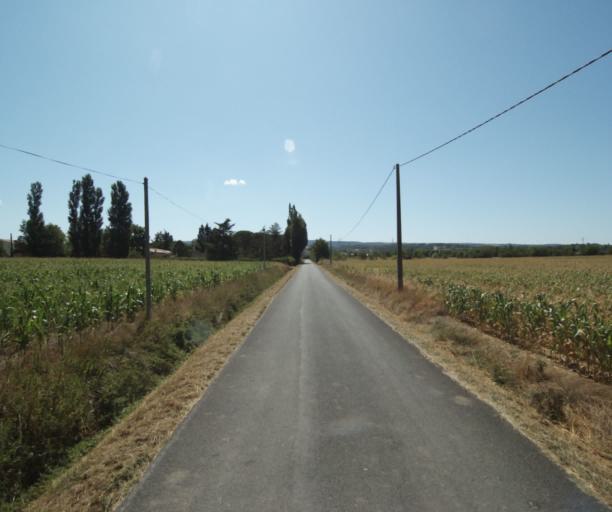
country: FR
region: Midi-Pyrenees
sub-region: Departement de la Haute-Garonne
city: Revel
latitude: 43.4608
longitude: 1.9708
